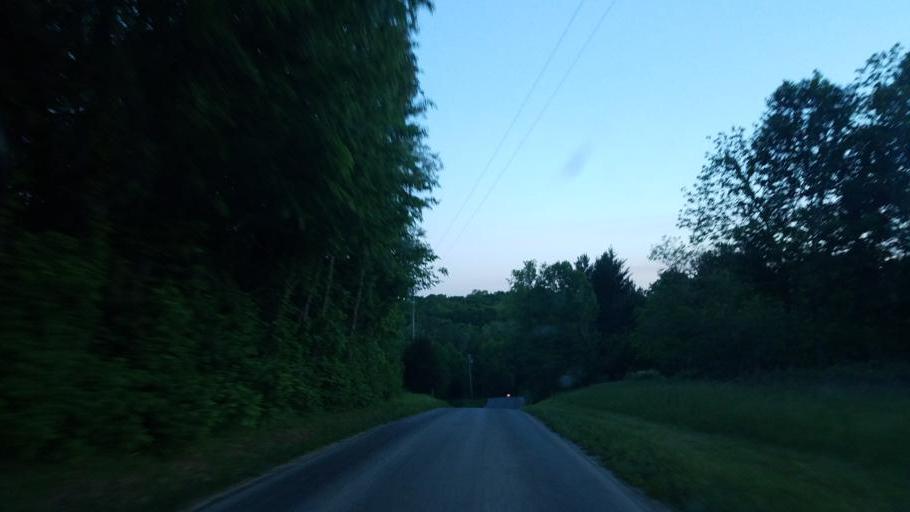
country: US
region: Ohio
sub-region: Highland County
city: Greenfield
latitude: 39.2014
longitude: -83.3795
